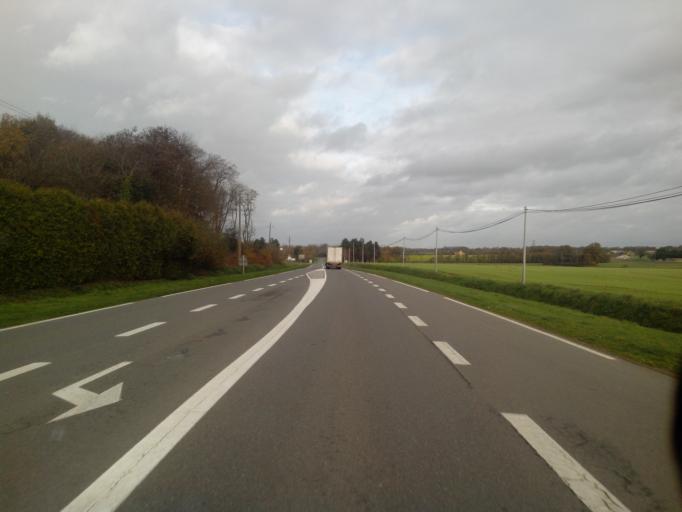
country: FR
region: Brittany
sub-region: Departement d'Ille-et-Vilaine
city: Gael
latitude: 48.1429
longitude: -2.2188
